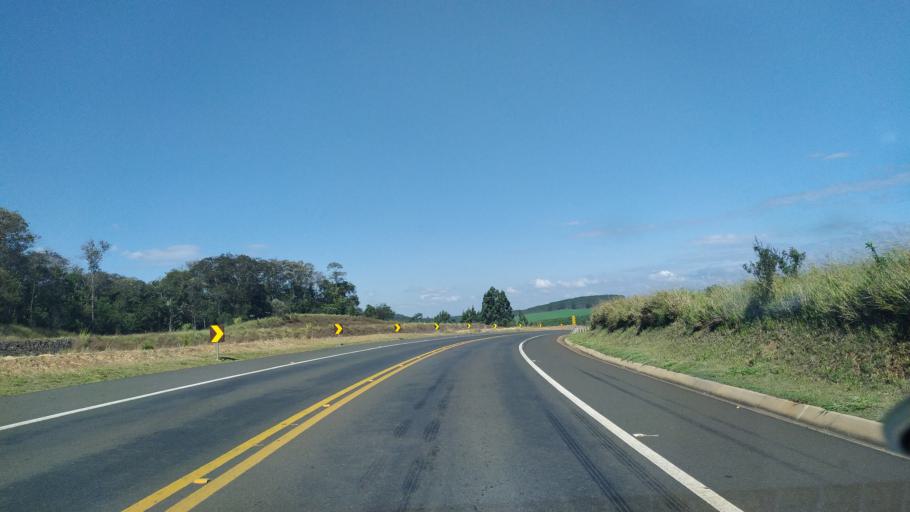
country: BR
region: Parana
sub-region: Ortigueira
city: Ortigueira
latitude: -24.2712
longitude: -50.8049
